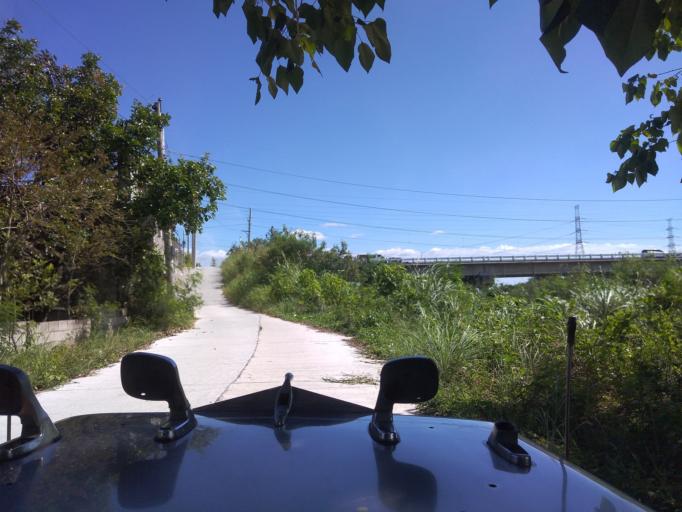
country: PH
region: Central Luzon
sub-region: Province of Pampanga
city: Bacolor
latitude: 15.0123
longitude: 120.6561
